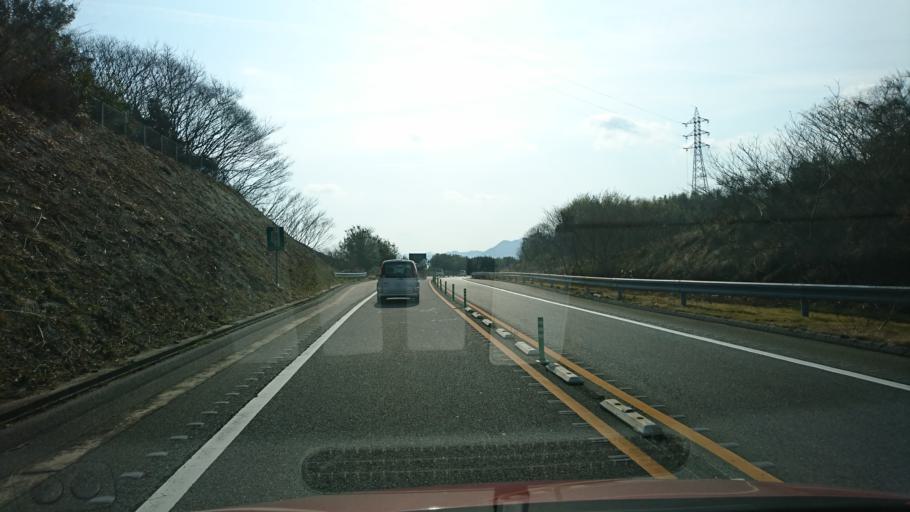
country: JP
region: Hiroshima
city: Onomichi
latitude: 34.3657
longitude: 133.1917
